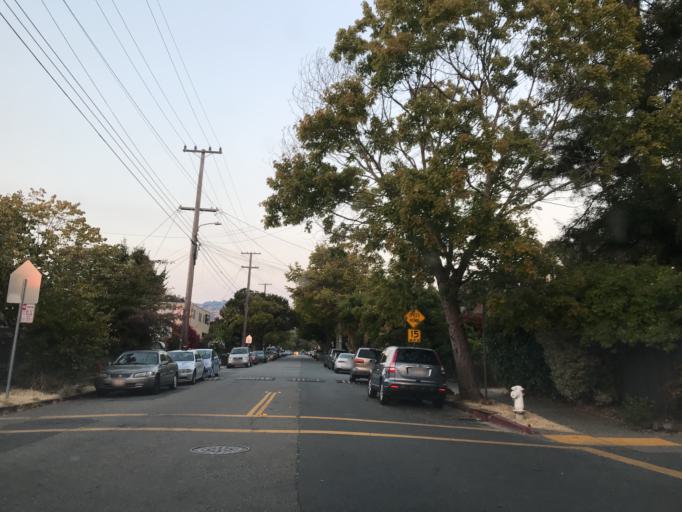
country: US
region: California
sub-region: Alameda County
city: Berkeley
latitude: 37.8689
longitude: -122.2863
